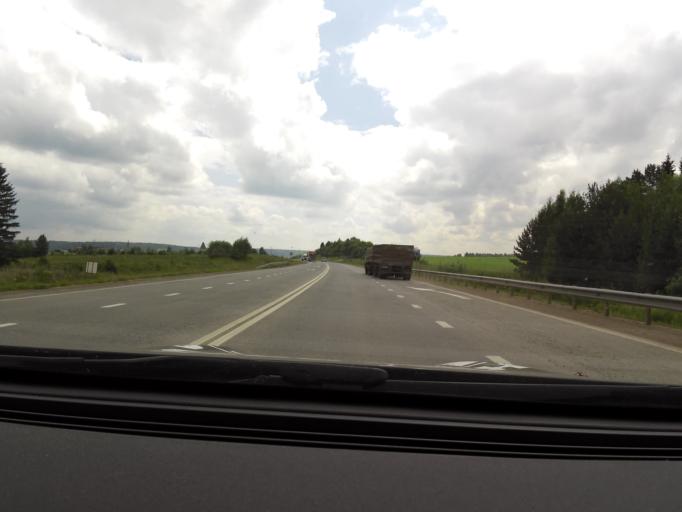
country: RU
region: Perm
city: Kungur
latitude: 57.3817
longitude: 56.9058
